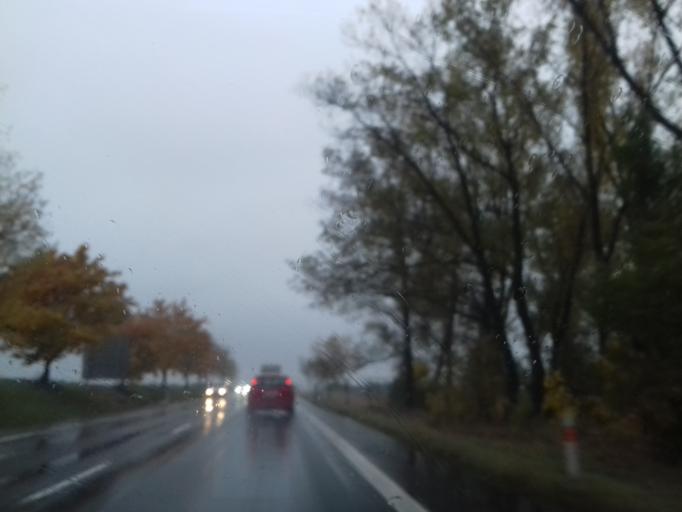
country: CZ
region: Pardubicky
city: Opatov
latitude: 49.7767
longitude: 16.5195
